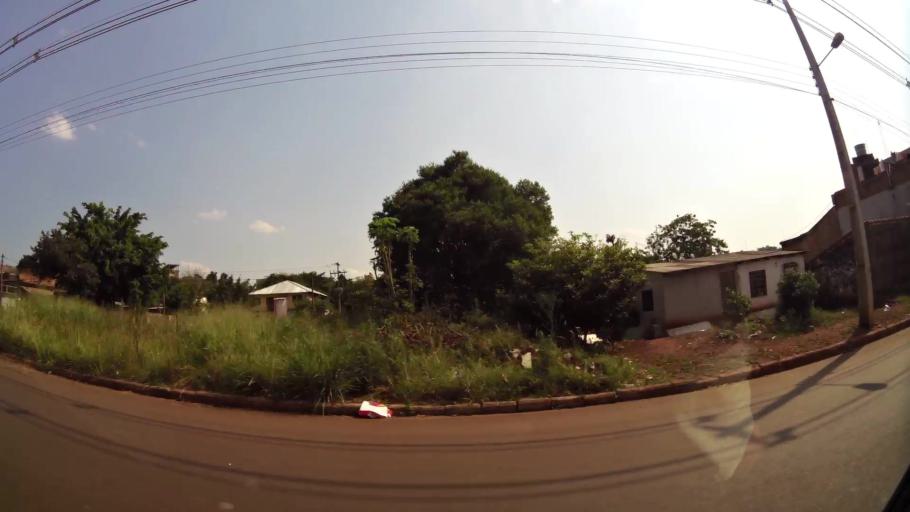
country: PY
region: Alto Parana
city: Ciudad del Este
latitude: -25.5062
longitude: -54.6247
